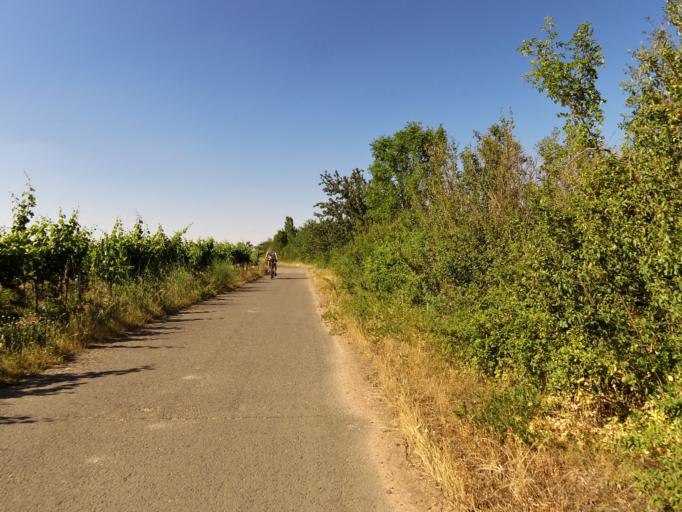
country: DE
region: Rheinland-Pfalz
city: Friedelsheim
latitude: 49.4386
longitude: 8.2043
